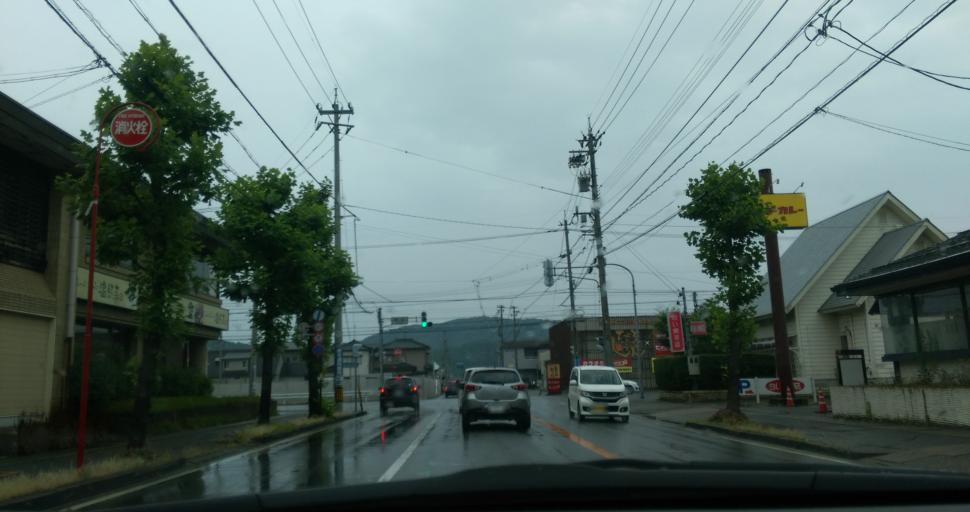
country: JP
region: Fukui
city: Fukui-shi
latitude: 36.0377
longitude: 136.1883
